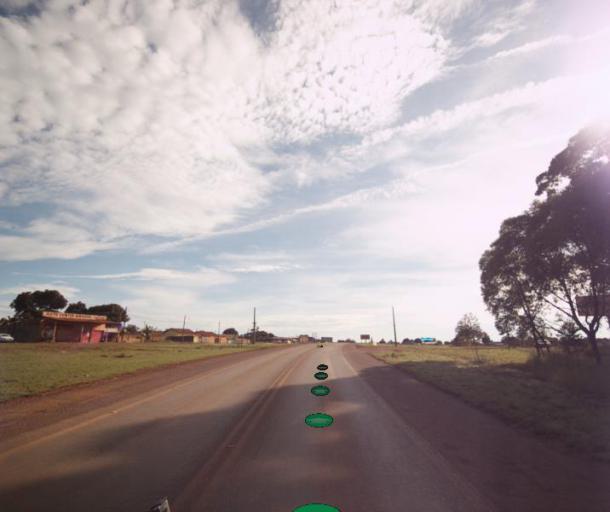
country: BR
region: Federal District
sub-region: Brasilia
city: Brasilia
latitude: -15.7402
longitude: -48.4094
